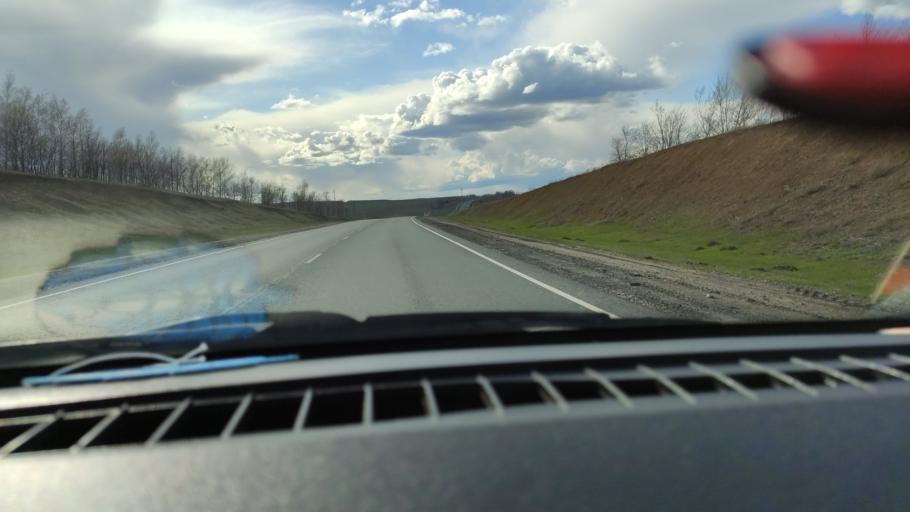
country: RU
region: Saratov
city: Shikhany
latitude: 52.1176
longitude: 47.2785
